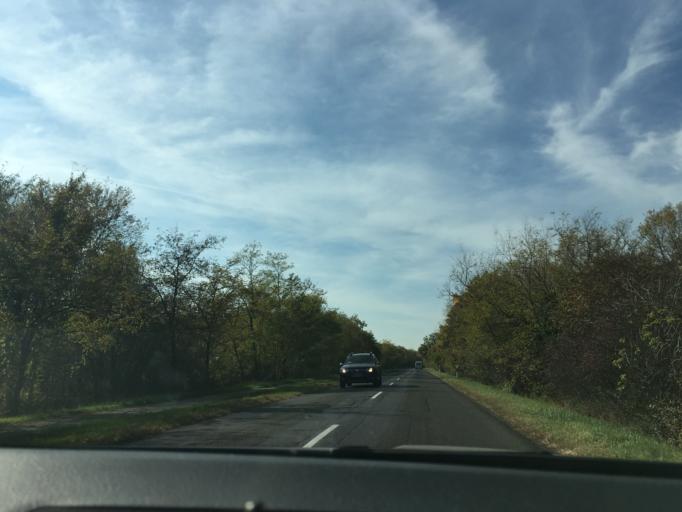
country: HU
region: Hajdu-Bihar
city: Vamospercs
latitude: 47.5257
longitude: 21.9500
